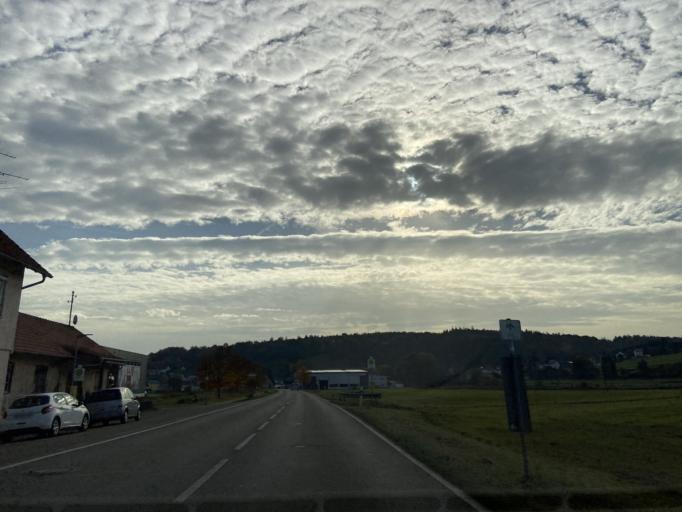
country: DE
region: Baden-Wuerttemberg
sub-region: Tuebingen Region
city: Bingen
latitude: 48.1081
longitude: 9.2821
